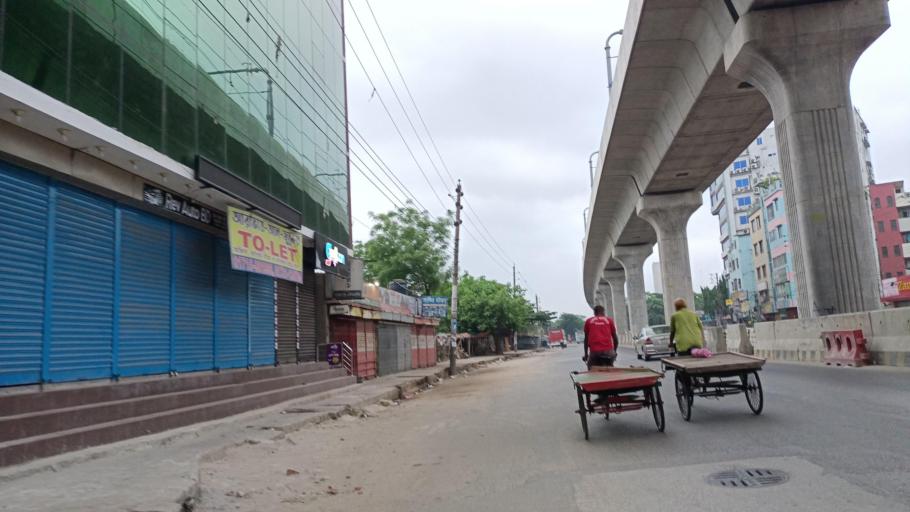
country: BD
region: Dhaka
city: Azimpur
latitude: 23.7853
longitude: 90.3779
